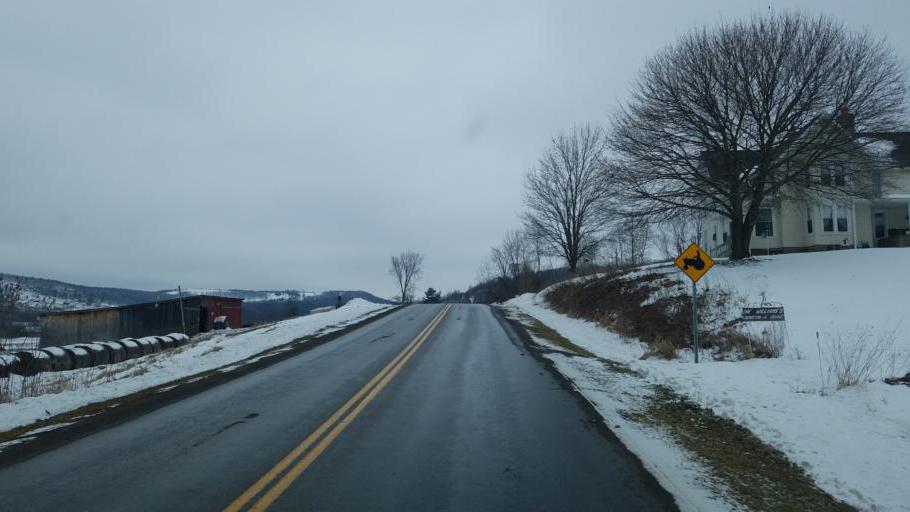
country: US
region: Pennsylvania
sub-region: Tioga County
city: Elkland
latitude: 42.0823
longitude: -77.4456
